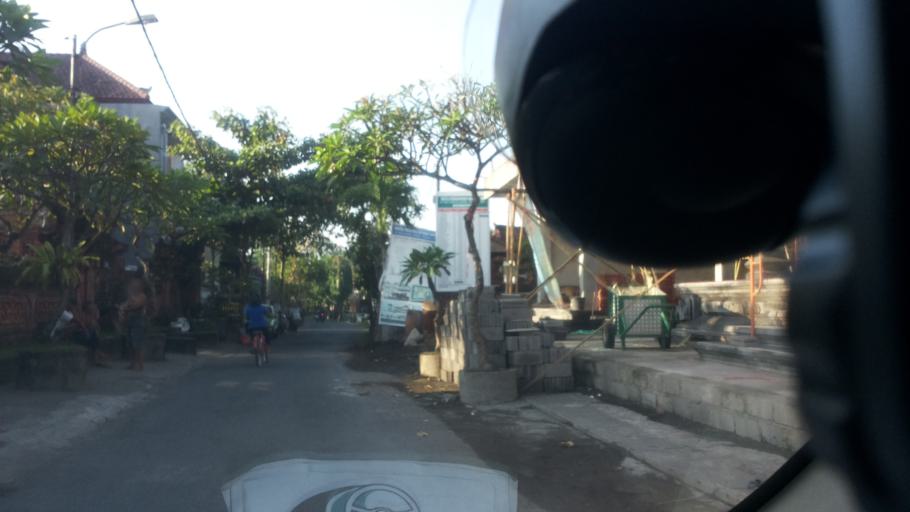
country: ID
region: Bali
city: Dajan Tangluk
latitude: -8.6446
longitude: 115.2415
